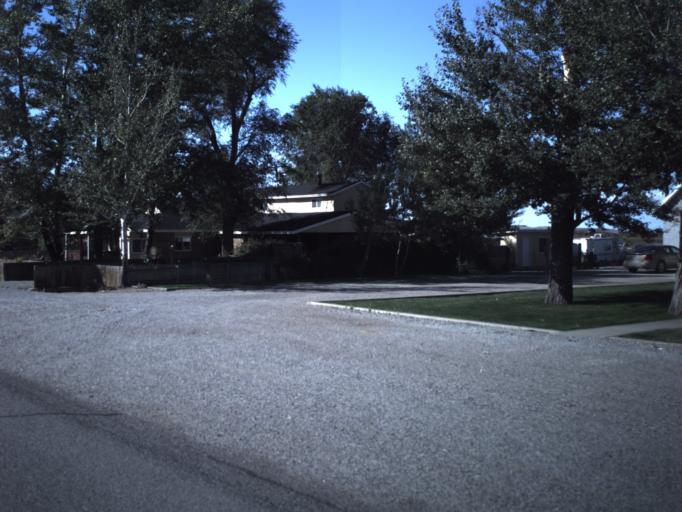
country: US
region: Utah
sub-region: Millard County
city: Delta
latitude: 39.2937
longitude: -112.6526
